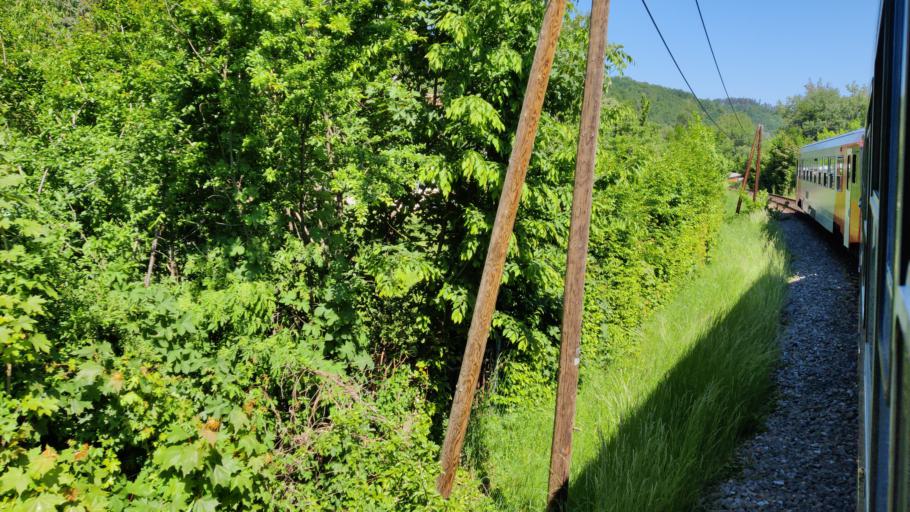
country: AT
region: Lower Austria
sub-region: Politischer Bezirk Horn
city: Gars am Kamp
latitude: 48.5934
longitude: 15.6575
